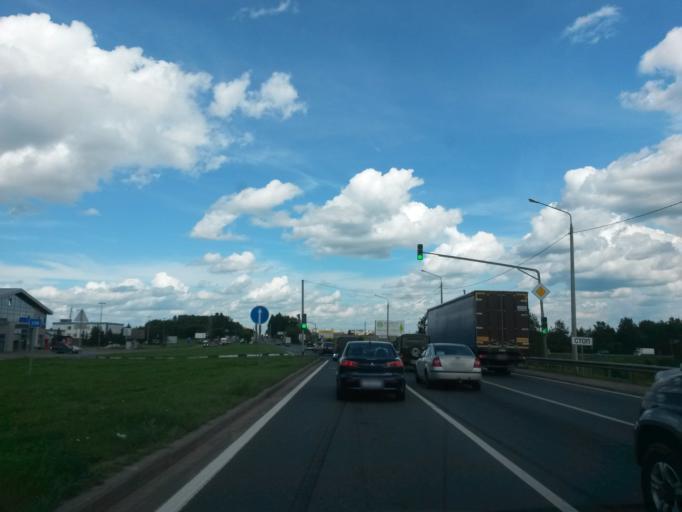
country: RU
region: Jaroslavl
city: Yaroslavl
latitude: 57.5631
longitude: 39.8271
